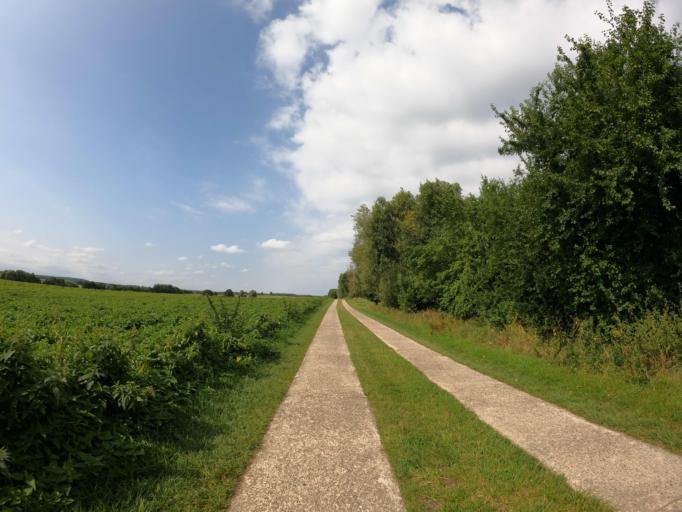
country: DE
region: Mecklenburg-Vorpommern
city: Malchow
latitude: 53.4382
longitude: 12.4857
